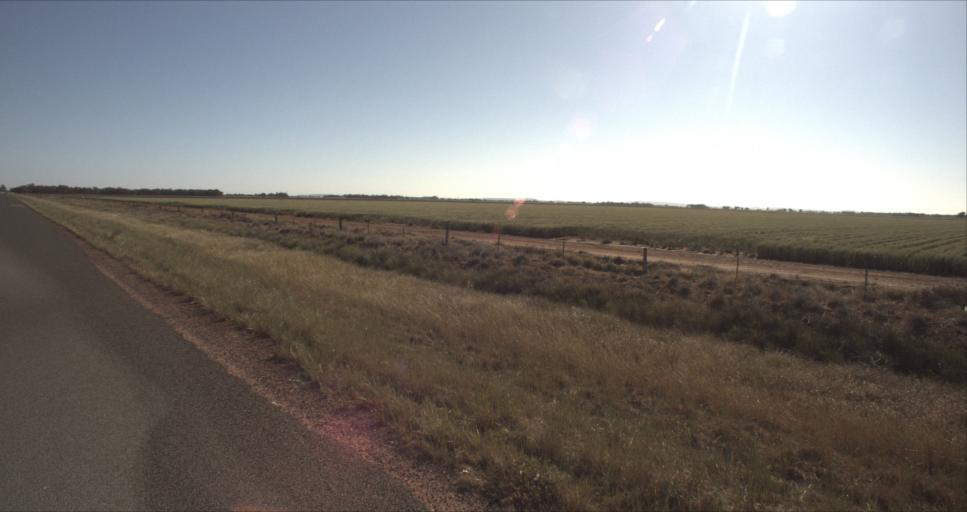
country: AU
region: New South Wales
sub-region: Leeton
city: Leeton
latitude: -34.5753
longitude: 146.2627
